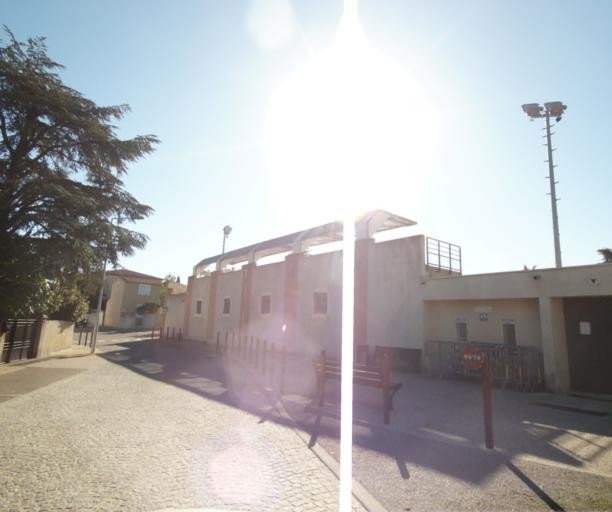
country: FR
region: Languedoc-Roussillon
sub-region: Departement du Gard
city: Bouillargues
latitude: 43.7992
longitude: 4.4233
